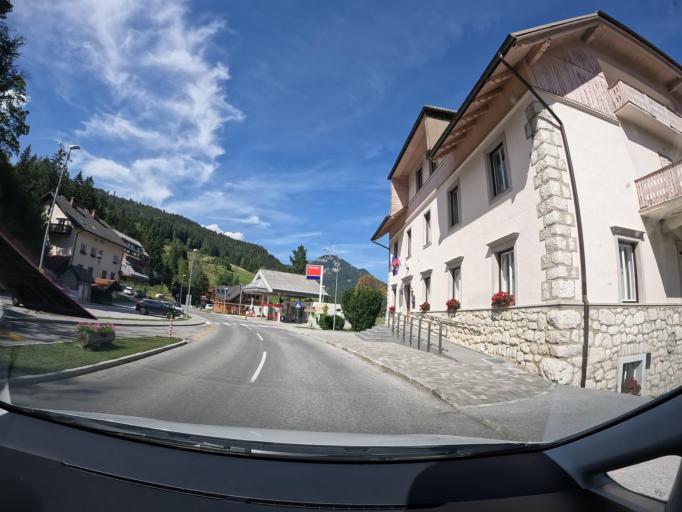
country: AT
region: Carinthia
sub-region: Politischer Bezirk Klagenfurt Land
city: Moosburg
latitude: 46.6774
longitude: 14.1251
